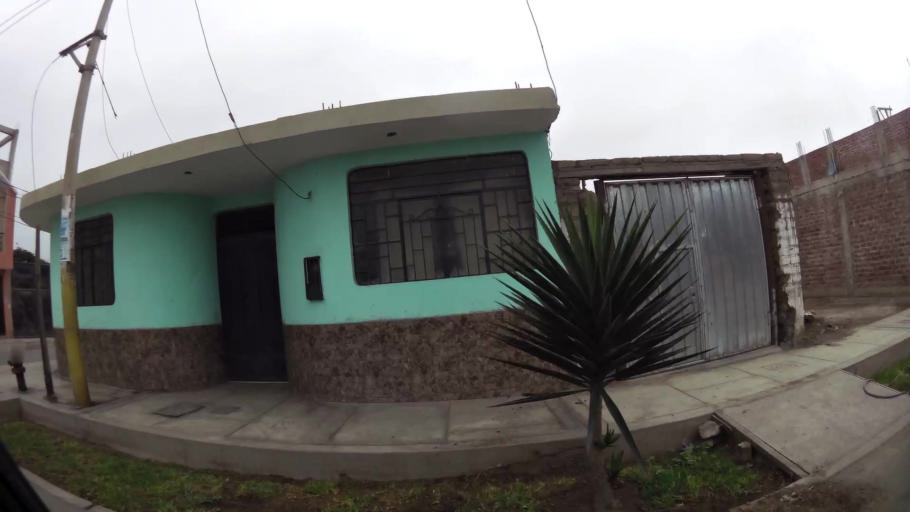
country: PE
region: Lima
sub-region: Barranca
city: Barranca
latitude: -10.7532
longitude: -77.7537
